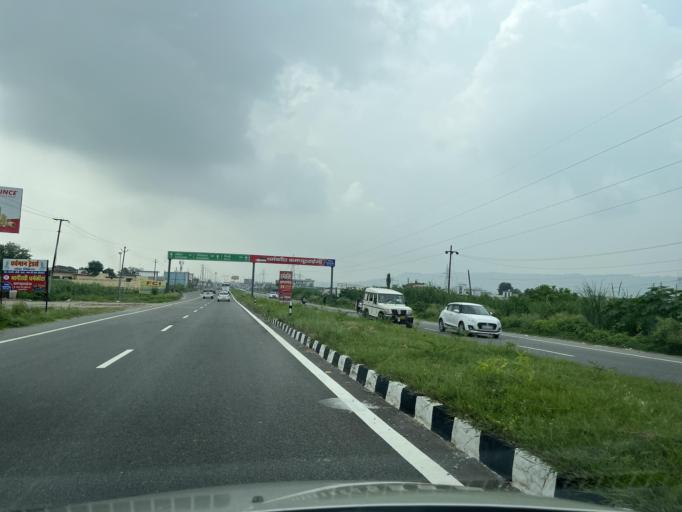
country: IN
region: Uttarakhand
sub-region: Dehradun
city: Raiwala
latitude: 30.0848
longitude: 78.1888
